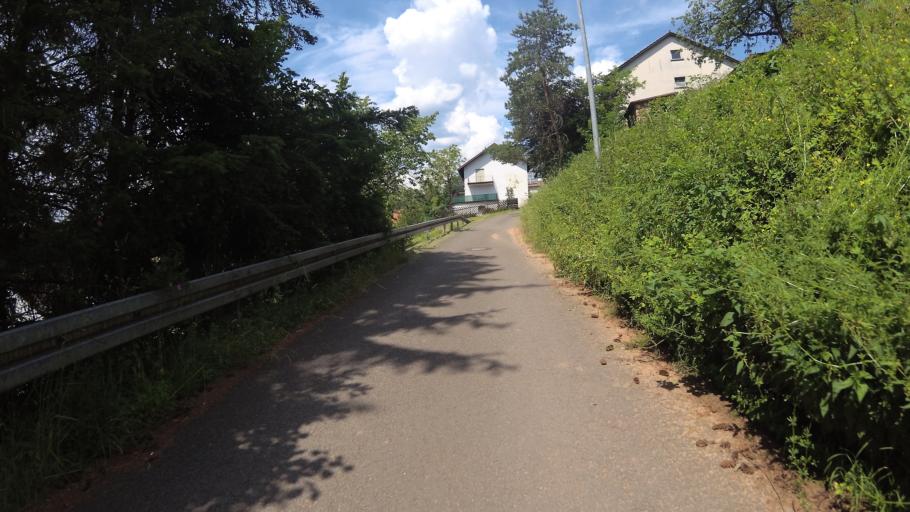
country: DE
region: Saarland
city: Homburg
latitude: 49.2977
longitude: 7.3662
